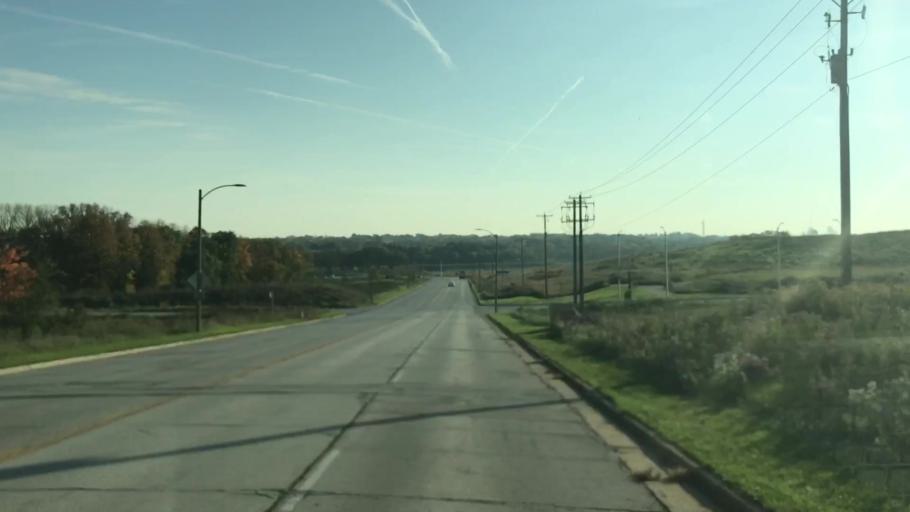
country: US
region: Wisconsin
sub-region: Milwaukee County
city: Wauwatosa
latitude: 43.0517
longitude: -88.0355
